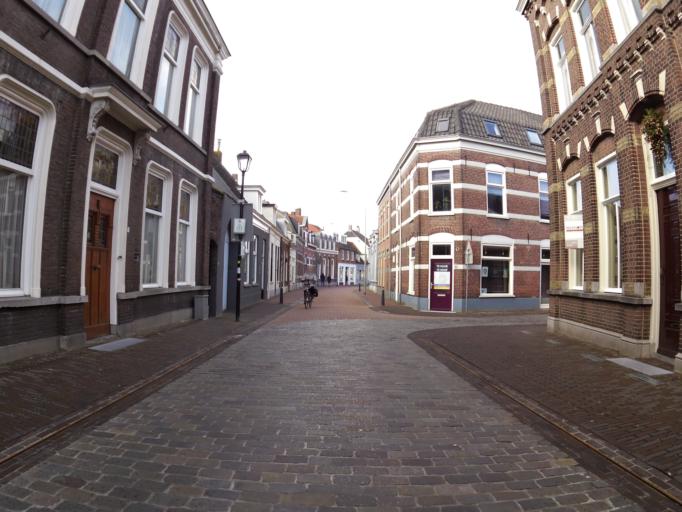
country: NL
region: North Brabant
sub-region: Gemeente Boxtel
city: Boxtel
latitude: 51.5891
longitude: 5.3260
